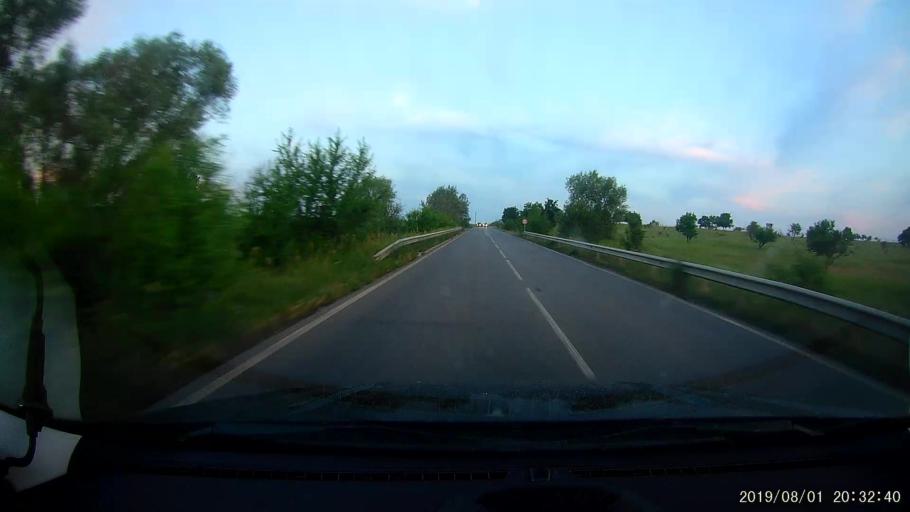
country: BG
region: Yambol
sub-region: Obshtina Elkhovo
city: Elkhovo
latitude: 42.1185
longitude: 26.5303
